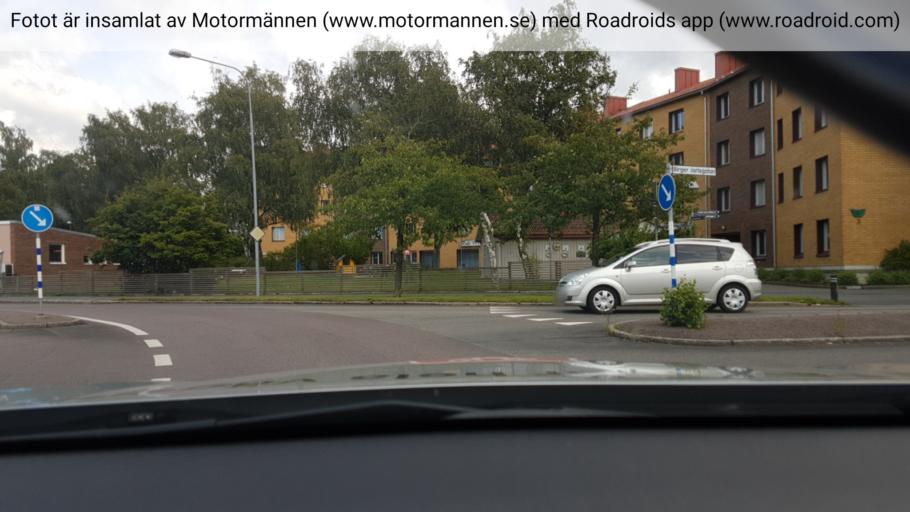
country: SE
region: Joenkoeping
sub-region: Jonkopings Kommun
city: Huskvarna
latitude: 57.7850
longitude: 14.2360
